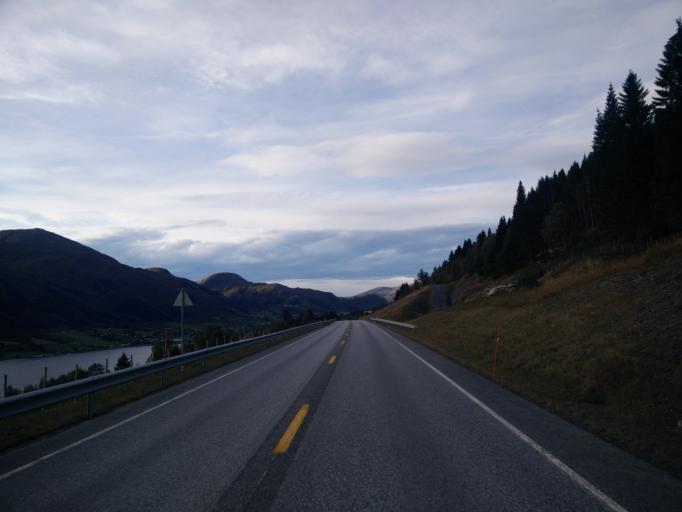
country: NO
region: More og Romsdal
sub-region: Gjemnes
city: Batnfjordsora
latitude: 62.9156
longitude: 7.6918
